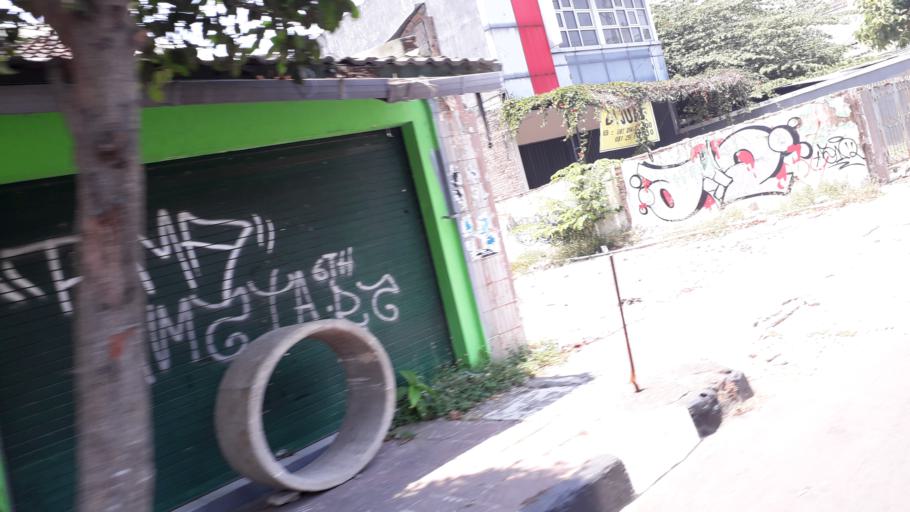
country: ID
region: Daerah Istimewa Yogyakarta
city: Yogyakarta
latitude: -7.7716
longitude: 110.3684
